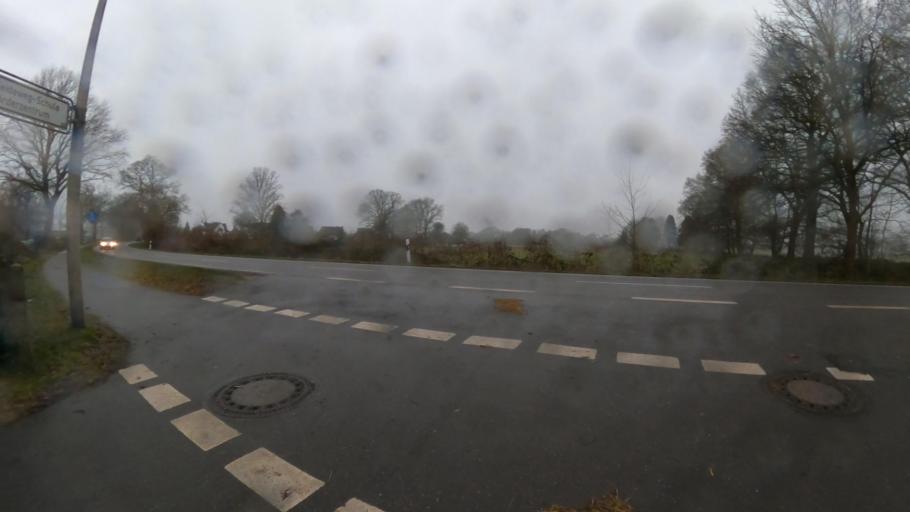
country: DE
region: Schleswig-Holstein
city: Appen
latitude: 53.6349
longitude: 9.7566
